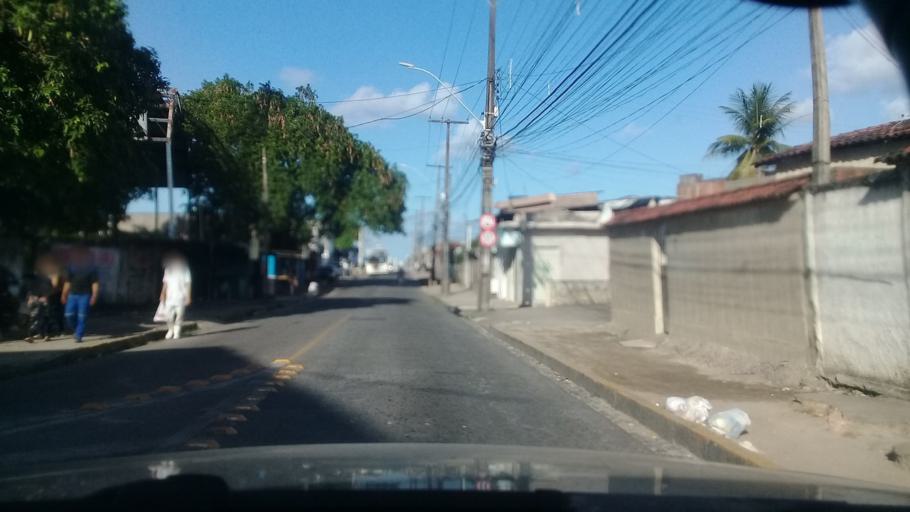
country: BR
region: Pernambuco
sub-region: Jaboatao Dos Guararapes
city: Jaboatao dos Guararapes
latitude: -8.1153
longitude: -34.9496
